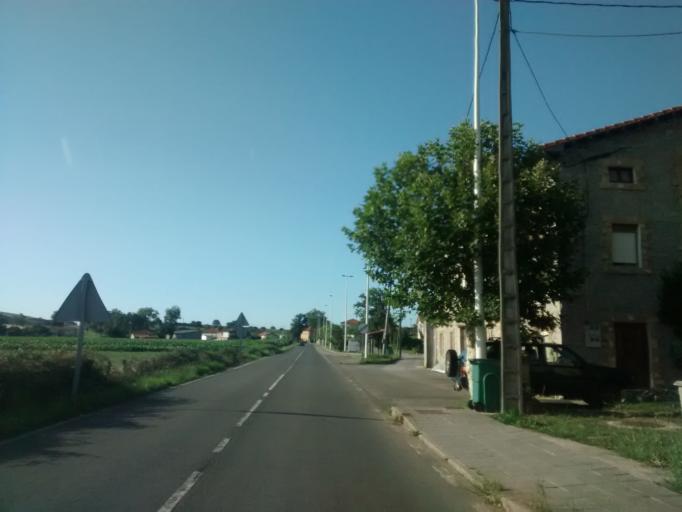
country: ES
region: Cantabria
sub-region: Provincia de Cantabria
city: Lierganes
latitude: 43.4004
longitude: -3.7367
